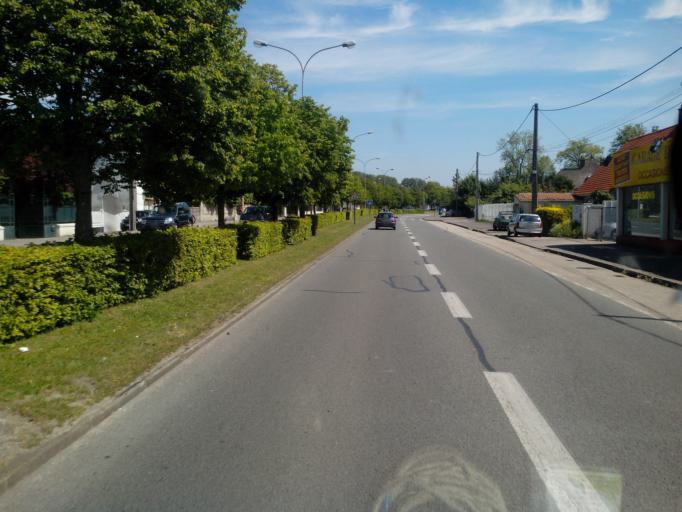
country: FR
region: Nord-Pas-de-Calais
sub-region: Departement du Pas-de-Calais
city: Saint-Etienne-au-Mont
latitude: 50.6844
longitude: 1.6301
